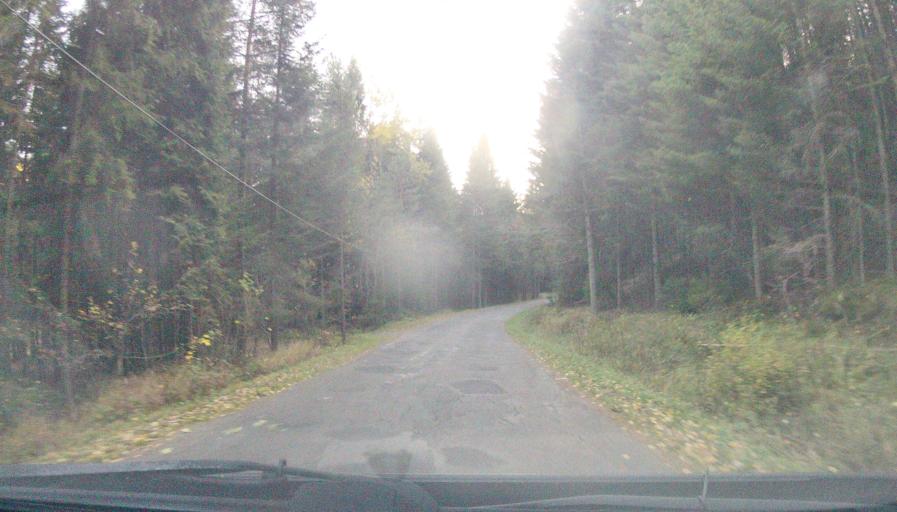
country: PL
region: Lesser Poland Voivodeship
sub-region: Powiat suski
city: Krzeszow
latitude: 49.7579
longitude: 19.4591
